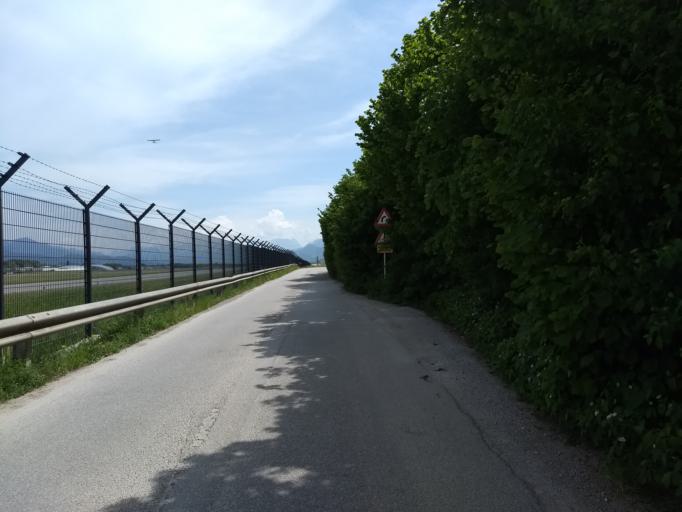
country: DE
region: Bavaria
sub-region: Upper Bavaria
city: Freilassing
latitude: 47.8018
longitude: 12.9953
